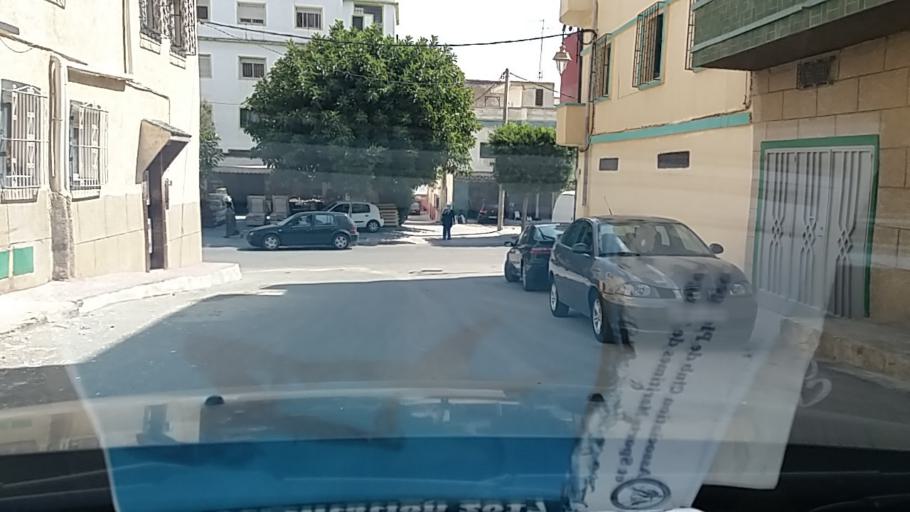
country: MA
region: Tanger-Tetouan
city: Tetouan
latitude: 35.5690
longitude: -5.3559
